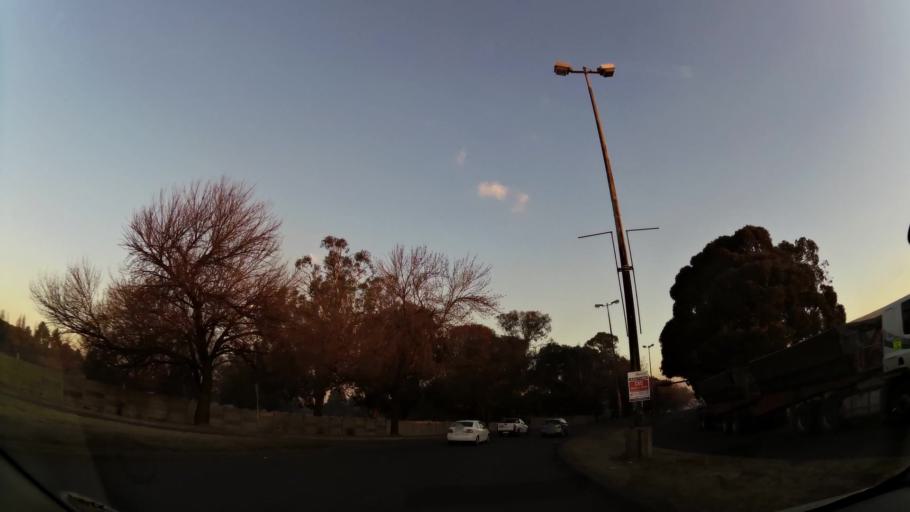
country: ZA
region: Mpumalanga
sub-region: Nkangala District Municipality
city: Witbank
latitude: -25.8779
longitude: 29.2096
